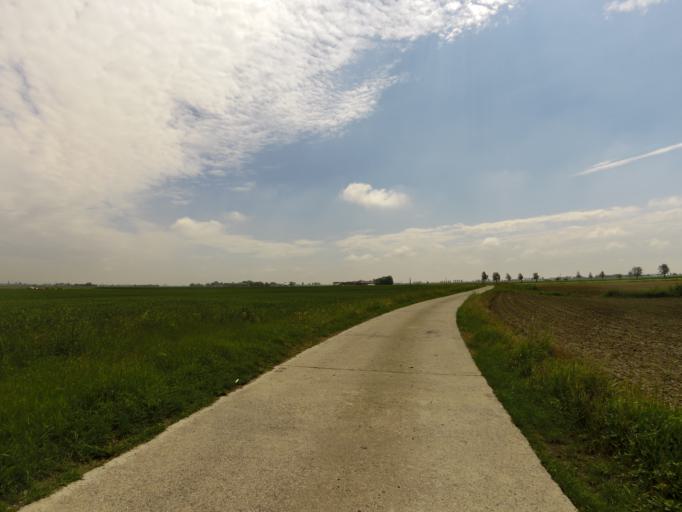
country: BE
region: Flanders
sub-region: Provincie West-Vlaanderen
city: Middelkerke
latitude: 51.1519
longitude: 2.8072
